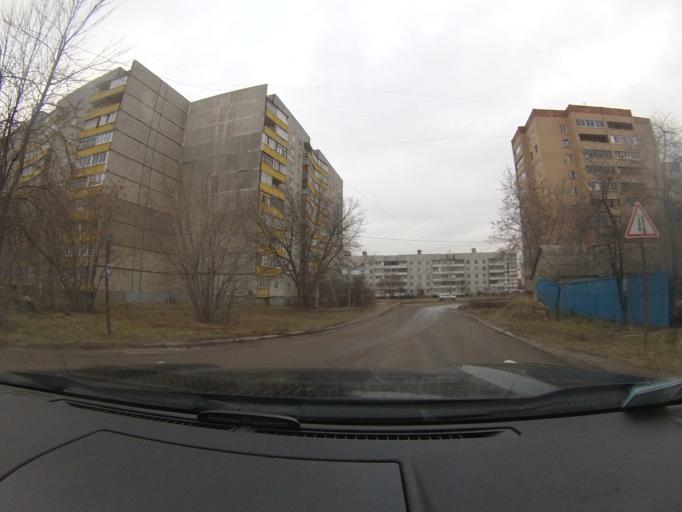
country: RU
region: Moskovskaya
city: Peski
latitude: 55.2699
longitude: 38.7536
